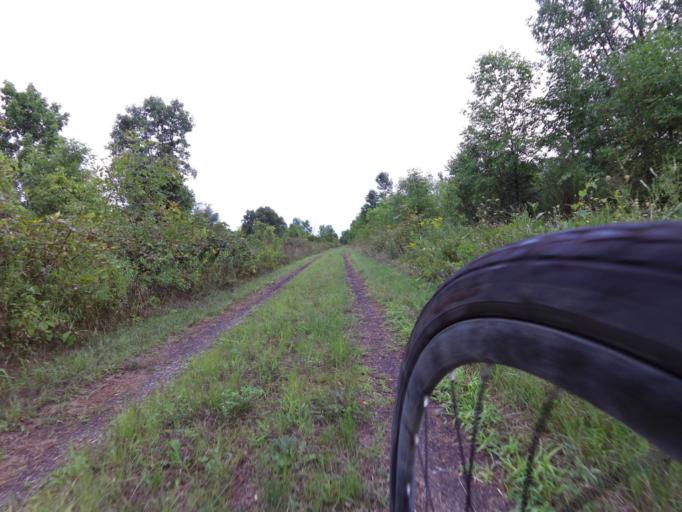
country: CA
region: Ontario
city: Perth
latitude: 44.6258
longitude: -76.2437
